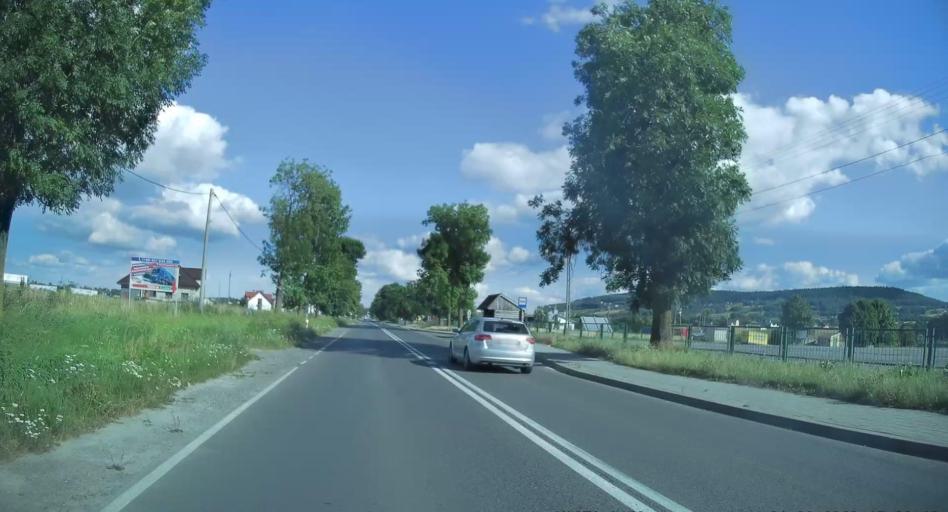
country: PL
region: Swietokrzyskie
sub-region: Powiat kielecki
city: Bodzentyn
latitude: 50.9497
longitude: 20.9295
